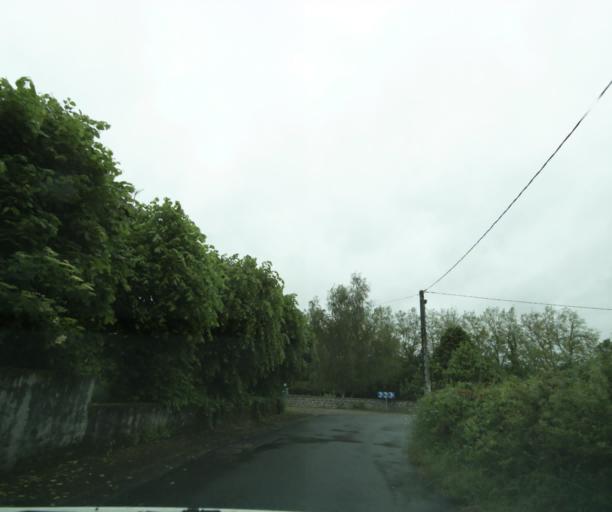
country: FR
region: Bourgogne
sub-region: Departement de Saone-et-Loire
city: Palinges
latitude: 46.5638
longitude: 4.2233
